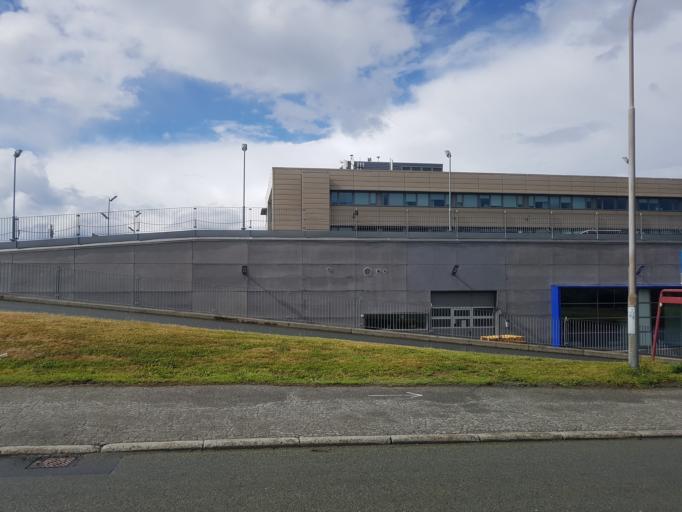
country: NO
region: Sor-Trondelag
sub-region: Trondheim
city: Trondheim
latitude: 63.4173
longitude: 10.4612
